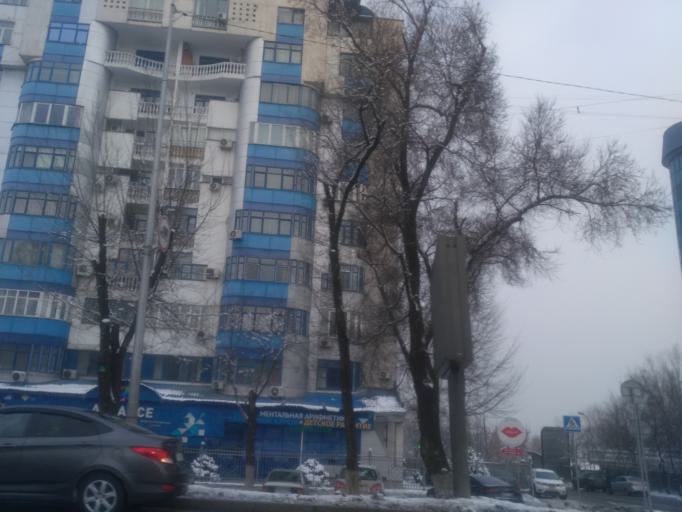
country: KZ
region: Almaty Qalasy
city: Almaty
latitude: 43.2241
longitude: 76.9378
